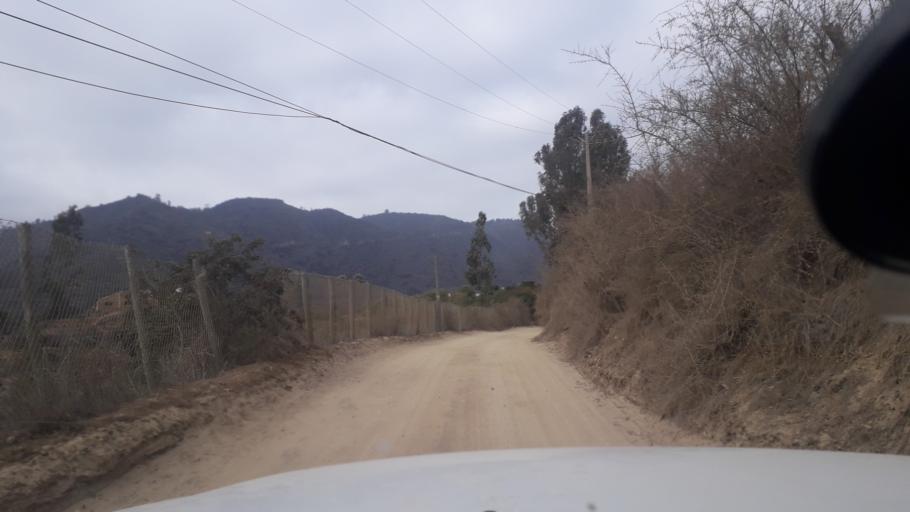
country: CL
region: Valparaiso
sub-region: Provincia de Valparaiso
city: Valparaiso
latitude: -33.1158
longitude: -71.6451
